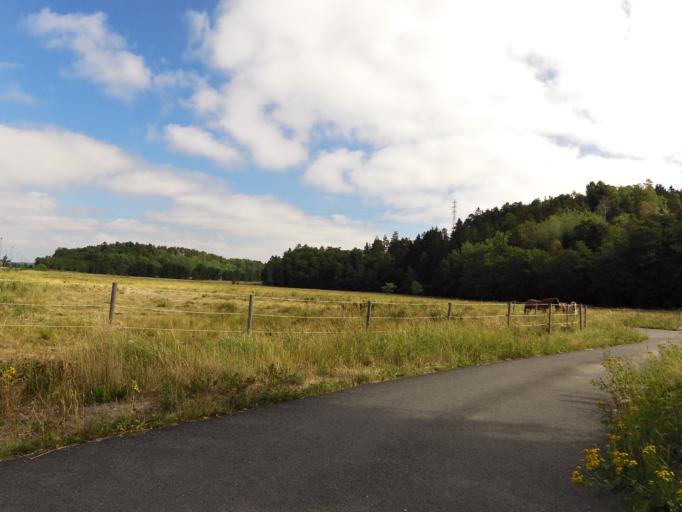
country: NO
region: Ostfold
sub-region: Fredrikstad
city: Fredrikstad
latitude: 59.2377
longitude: 10.9119
